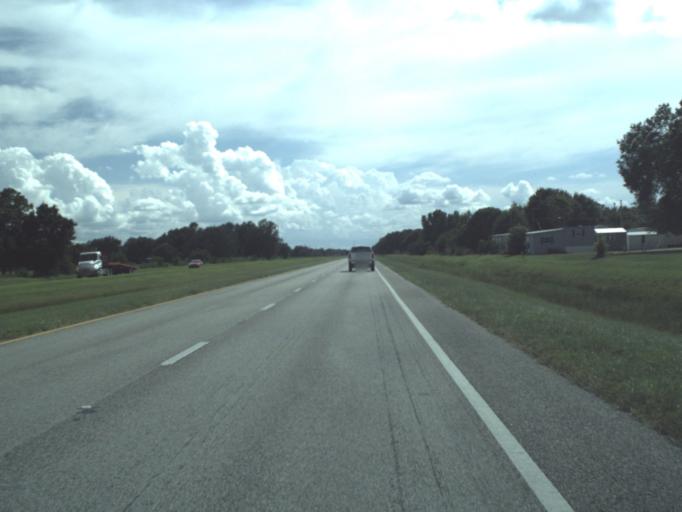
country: US
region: Florida
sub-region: DeSoto County
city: Arcadia
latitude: 27.2799
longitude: -81.8320
